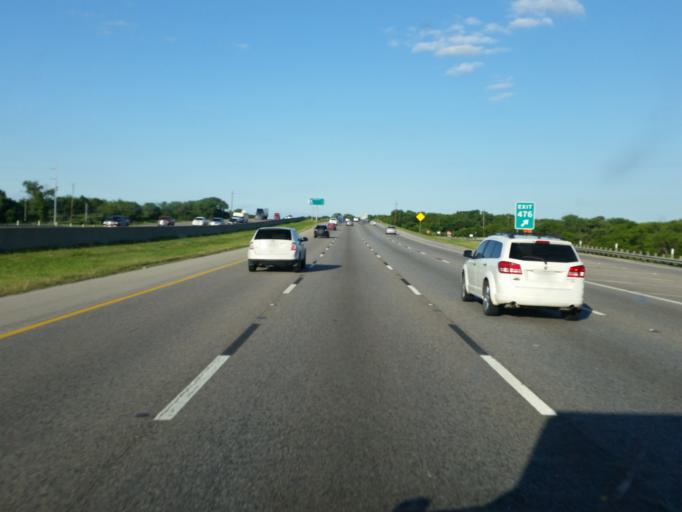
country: US
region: Texas
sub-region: Dallas County
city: Hutchins
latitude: 32.6784
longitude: -96.6798
